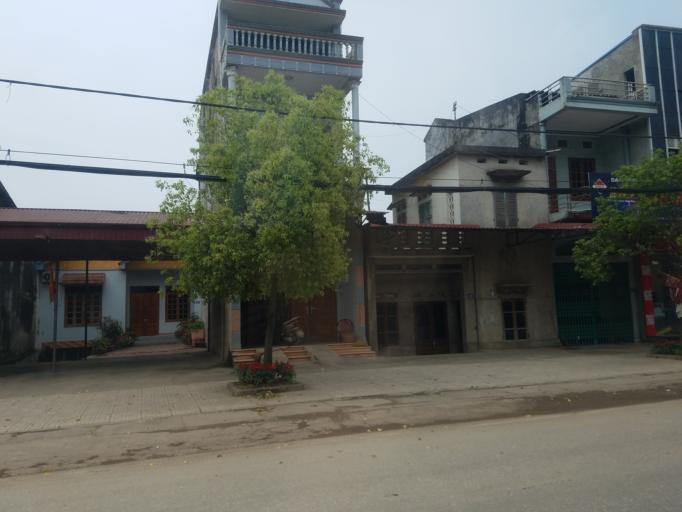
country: VN
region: Thai Nguyen
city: Chua Hang
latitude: 21.6145
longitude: 105.8393
